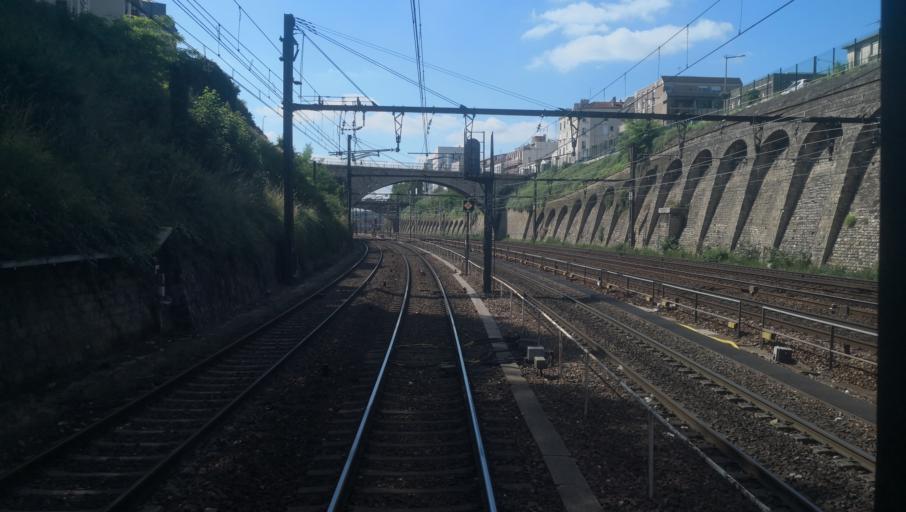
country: FR
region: Ile-de-France
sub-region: Departement du Val-de-Marne
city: Charenton-le-Pont
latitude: 48.8229
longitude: 2.4087
